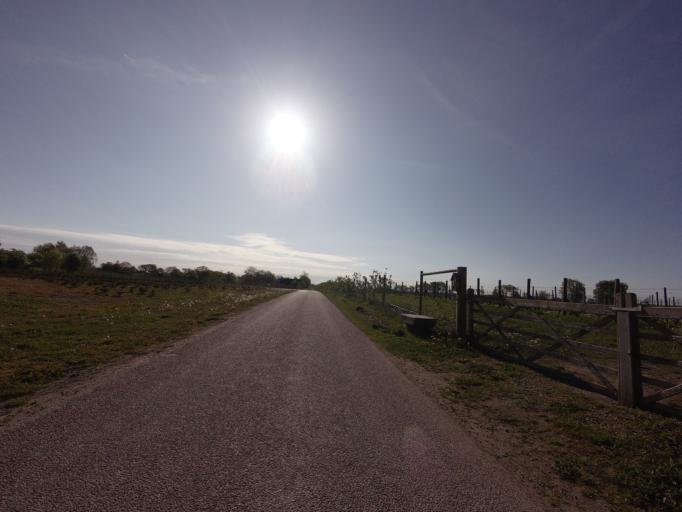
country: SE
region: Skane
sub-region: Hoganas Kommun
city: Hoganas
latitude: 56.2575
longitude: 12.5404
